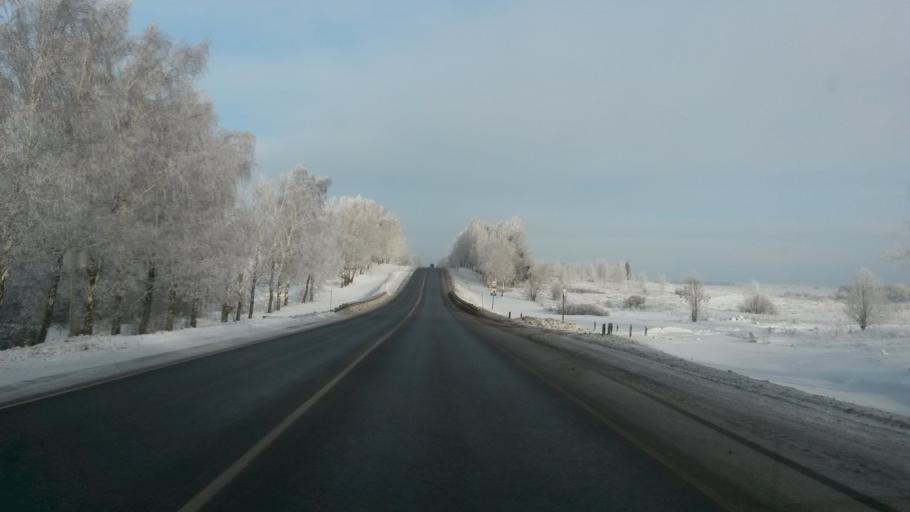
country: RU
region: Vladimir
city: Bogolyubovo
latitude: 56.2418
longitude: 40.4532
